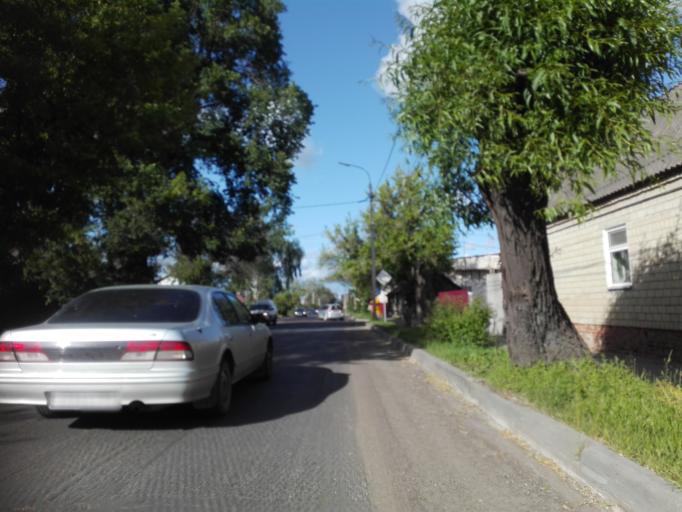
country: RU
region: Orjol
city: Orel
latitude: 52.9558
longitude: 36.0516
